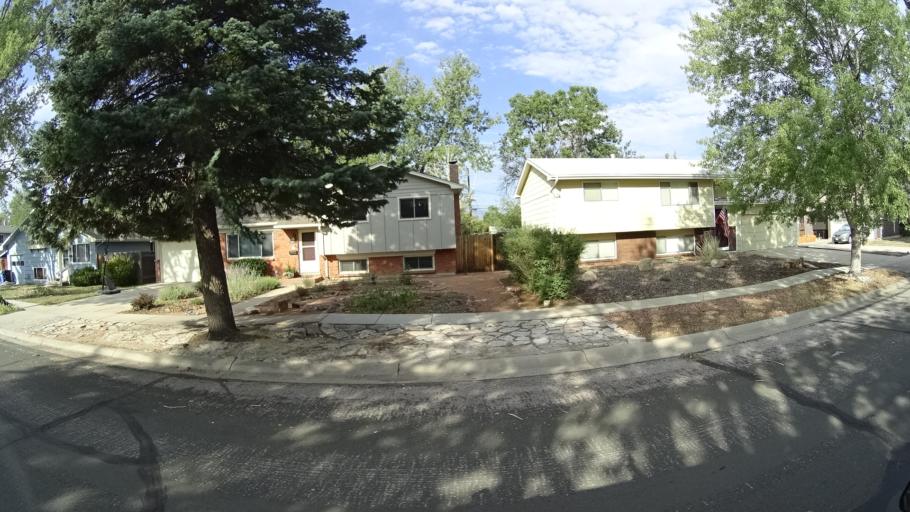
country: US
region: Colorado
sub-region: El Paso County
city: Cimarron Hills
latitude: 38.8568
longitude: -104.7622
